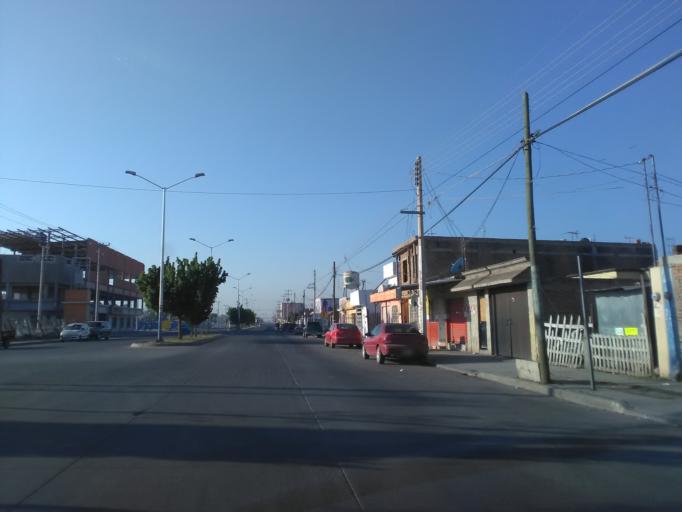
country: MX
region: Durango
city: Victoria de Durango
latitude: 24.0595
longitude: -104.6310
